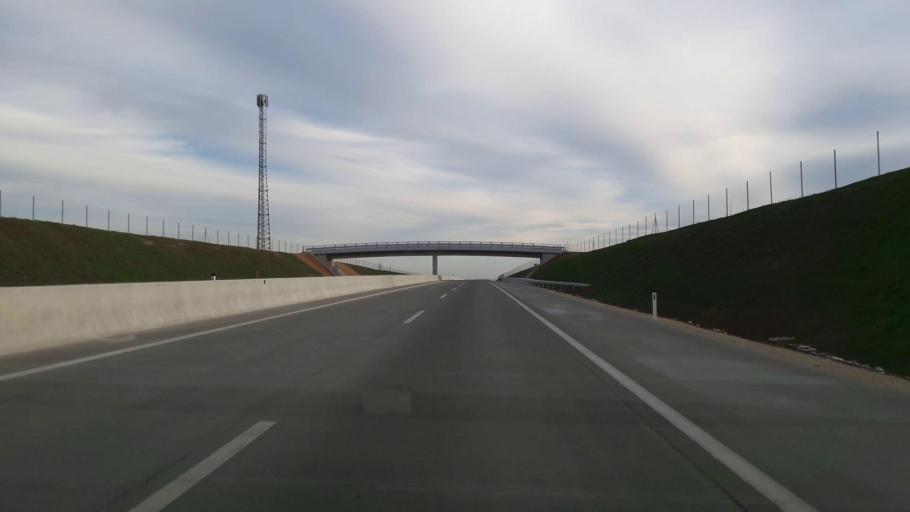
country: AT
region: Lower Austria
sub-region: Politischer Bezirk Mistelbach
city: Herrnbaumgarten
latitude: 48.6787
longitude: 16.6637
